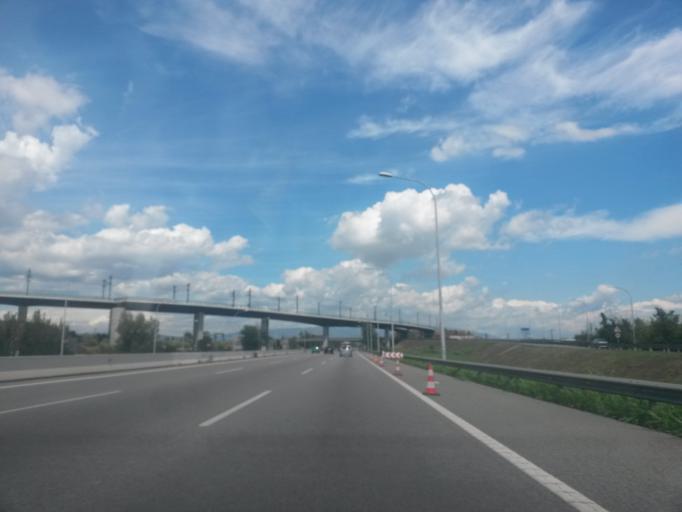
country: ES
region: Catalonia
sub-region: Provincia de Barcelona
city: Mollet del Valles
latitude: 41.5209
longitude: 2.2118
